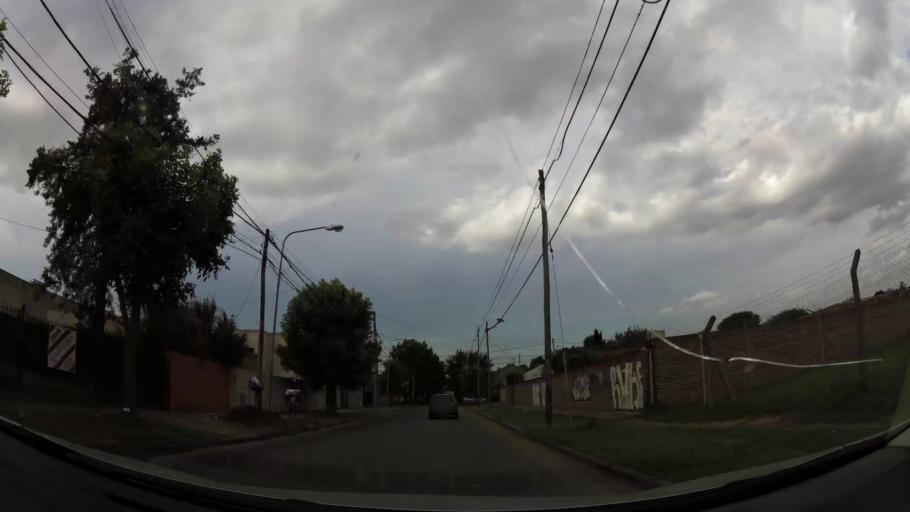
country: AR
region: Buenos Aires
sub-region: Partido de Tigre
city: Tigre
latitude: -34.4673
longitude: -58.6530
